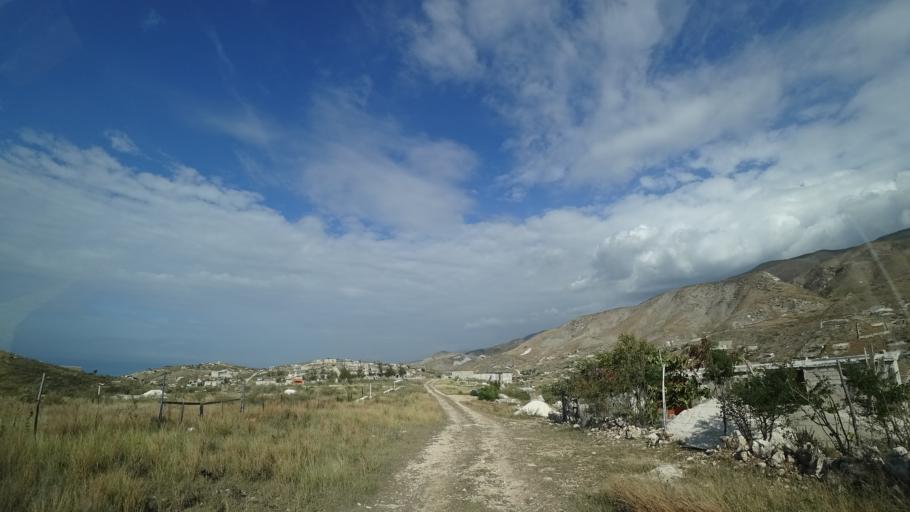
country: HT
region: Ouest
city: Croix des Bouquets
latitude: 18.6747
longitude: -72.2917
